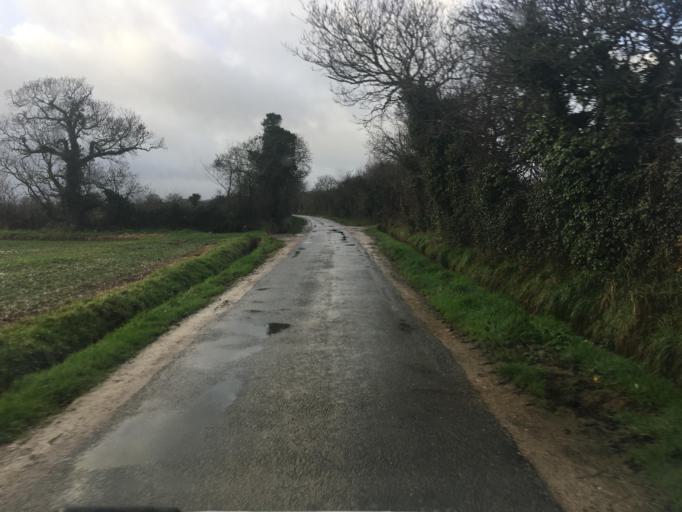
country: FR
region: Lower Normandy
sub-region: Departement de la Manche
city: Saint-Pierre-Eglise
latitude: 49.6730
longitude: -1.3219
